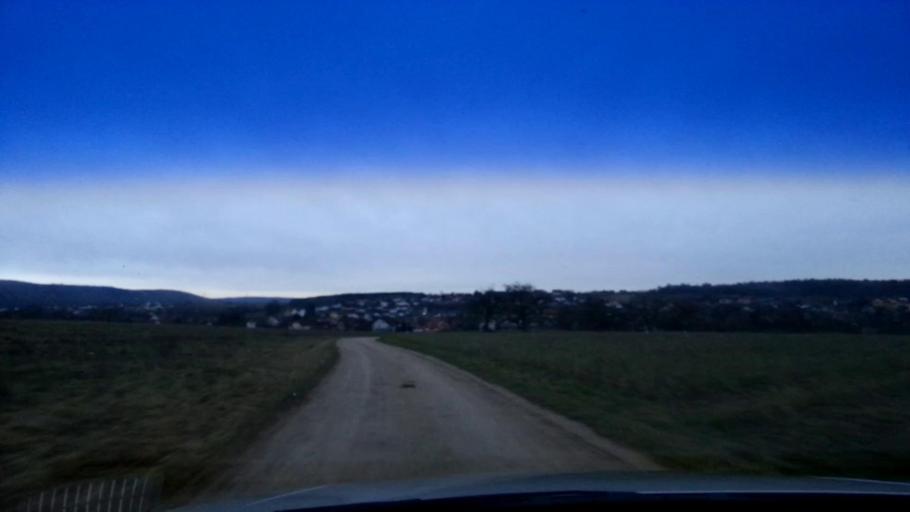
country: DE
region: Bavaria
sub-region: Upper Franconia
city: Litzendorf
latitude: 49.9163
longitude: 10.9906
